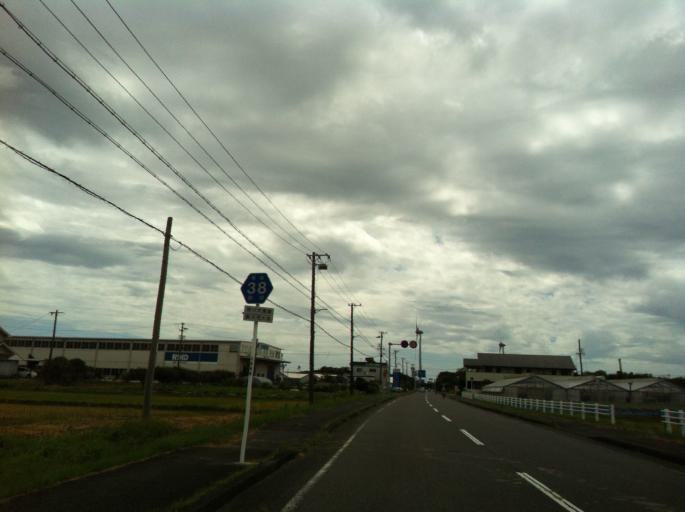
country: JP
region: Shizuoka
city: Kakegawa
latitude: 34.6638
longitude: 138.0449
